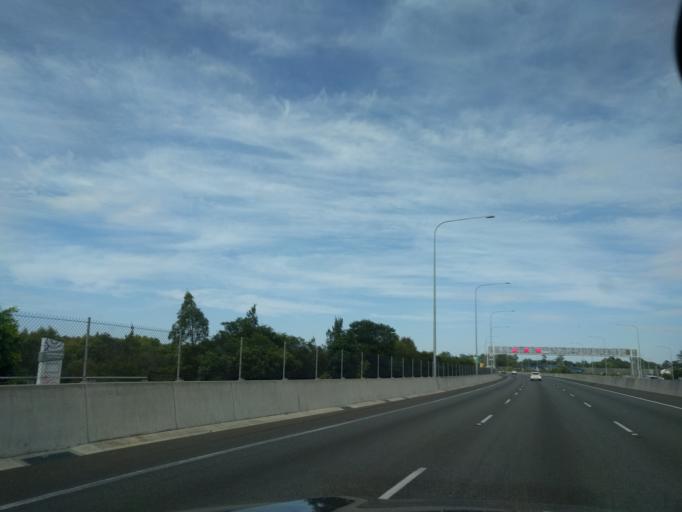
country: AU
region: Queensland
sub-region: Ipswich
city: Redbank
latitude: -27.6012
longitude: 152.8787
